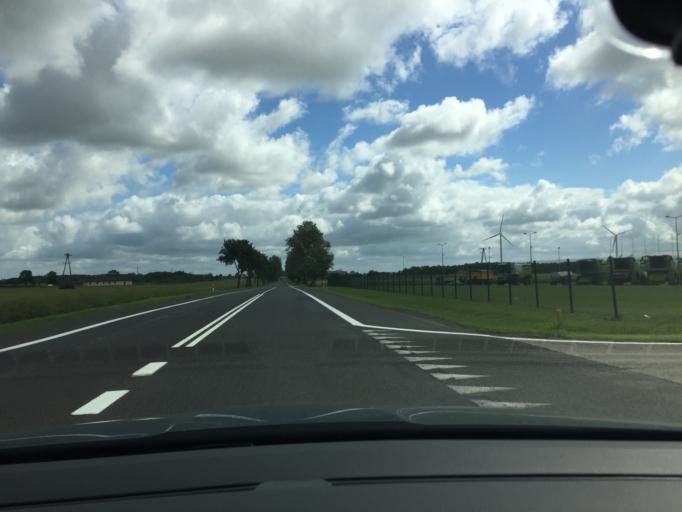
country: PL
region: West Pomeranian Voivodeship
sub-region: Powiat slawienski
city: Slawno
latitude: 54.3186
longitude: 16.5357
